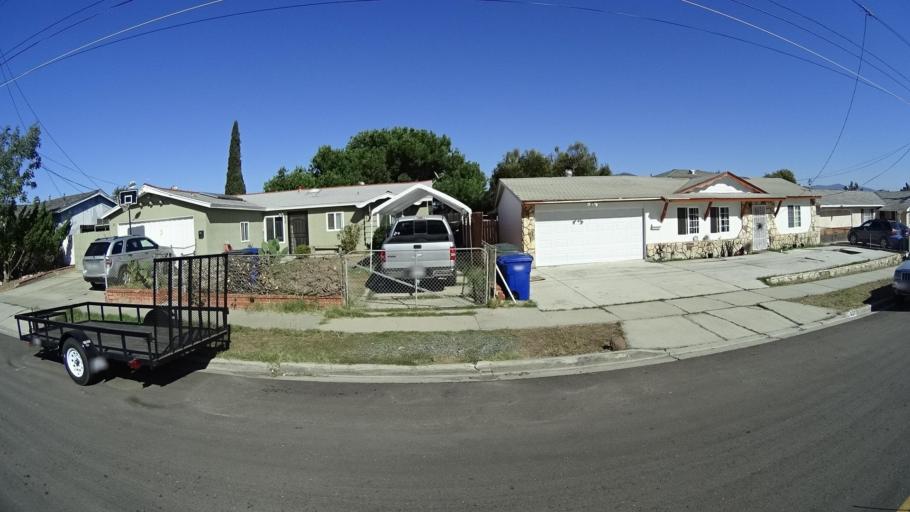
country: US
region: California
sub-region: San Diego County
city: La Presa
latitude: 32.7052
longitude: -117.0193
